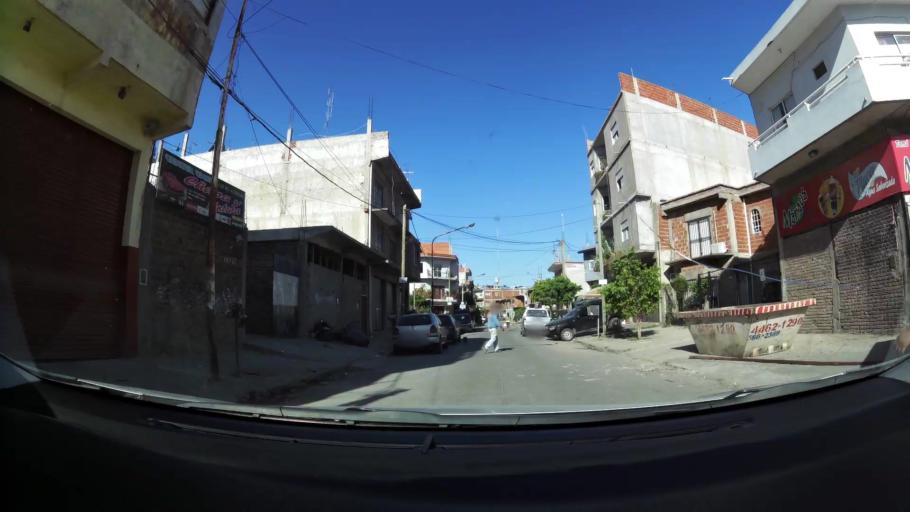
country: AR
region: Buenos Aires F.D.
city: Villa Lugano
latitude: -34.7028
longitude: -58.4812
